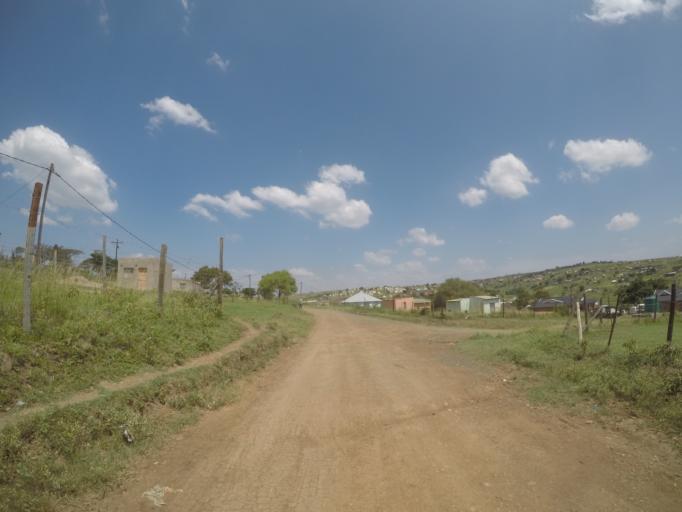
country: ZA
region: KwaZulu-Natal
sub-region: uThungulu District Municipality
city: Empangeni
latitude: -28.6030
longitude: 31.7409
